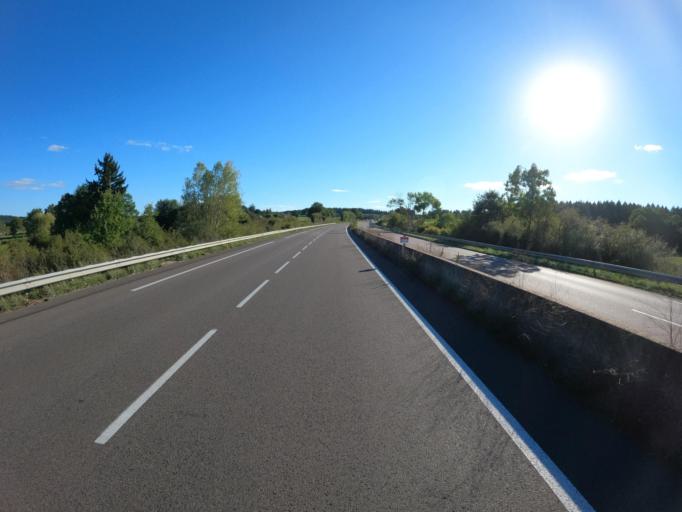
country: FR
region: Bourgogne
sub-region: Departement de Saone-et-Loire
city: Saint-Vallier
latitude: 46.6399
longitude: 4.3281
